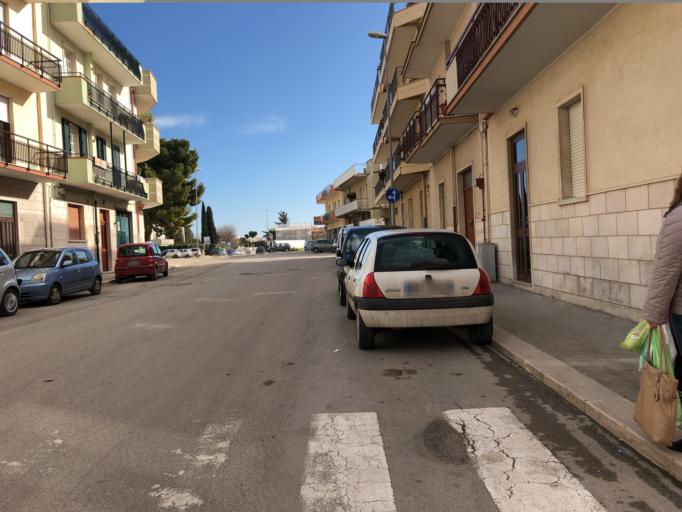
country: IT
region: Apulia
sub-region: Provincia di Barletta - Andria - Trani
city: Andria
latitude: 41.2236
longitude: 16.3074
